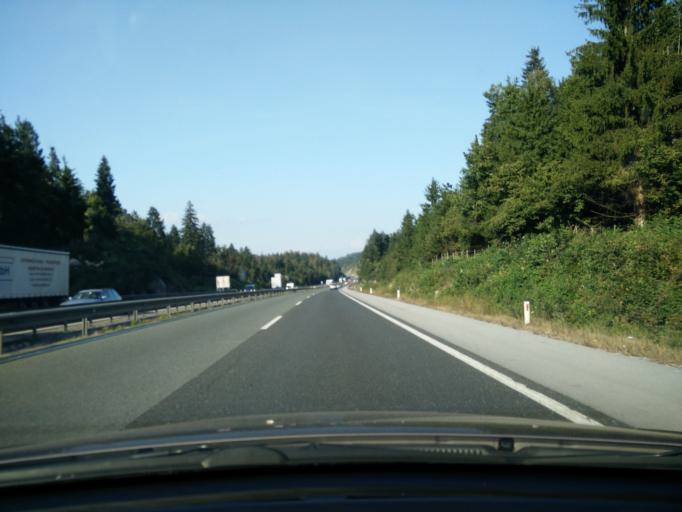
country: SI
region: Logatec
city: Logatec
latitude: 45.9123
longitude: 14.2604
